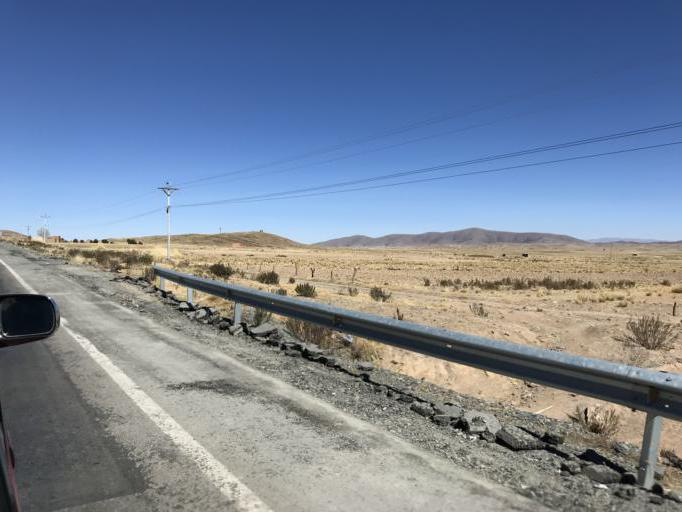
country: BO
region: La Paz
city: Batallas
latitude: -16.2620
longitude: -68.5593
